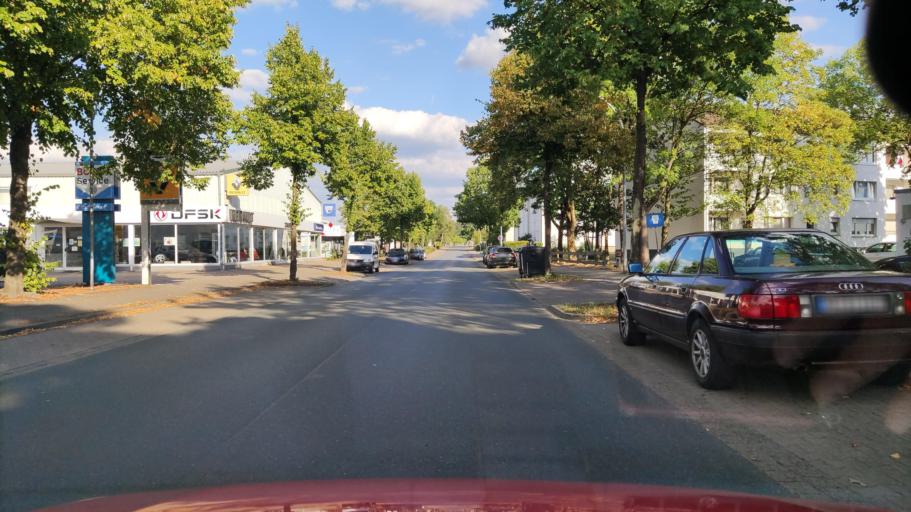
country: DE
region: Lower Saxony
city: Munster
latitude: 52.9910
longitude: 10.0997
